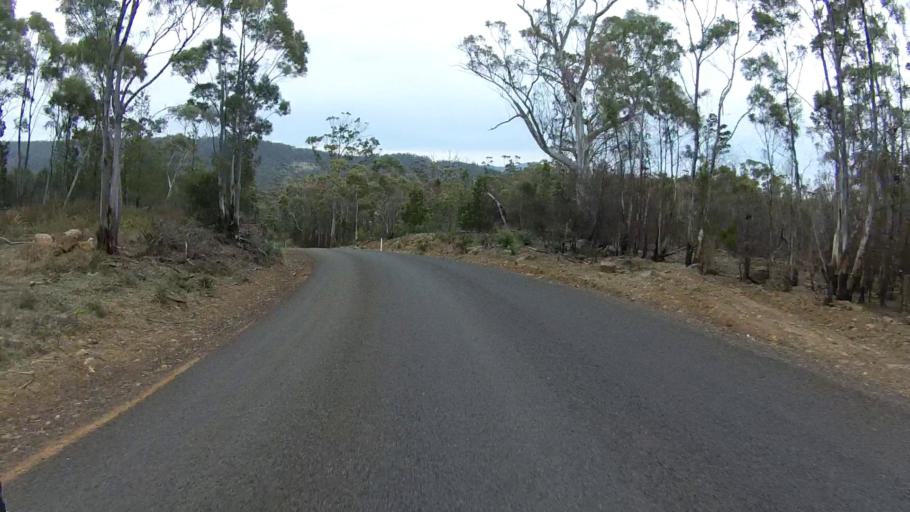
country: AU
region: Tasmania
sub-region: Sorell
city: Sorell
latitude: -42.5790
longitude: 147.8794
